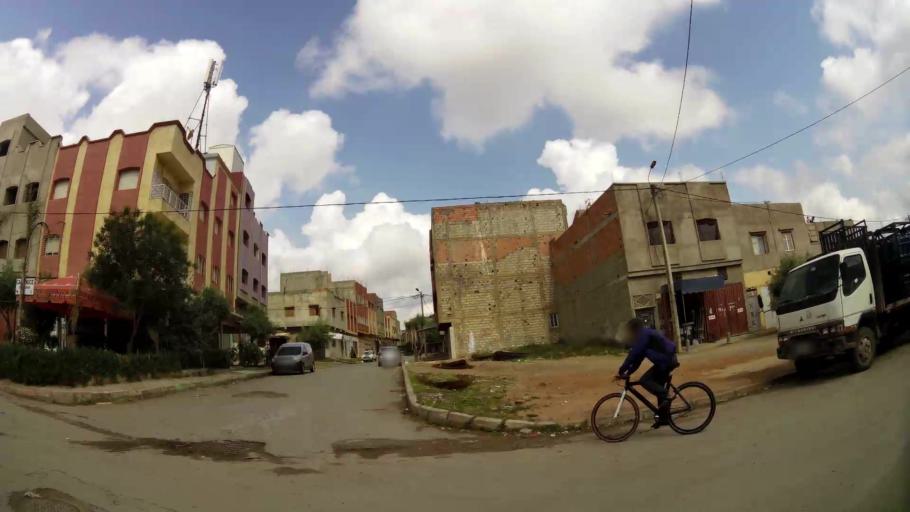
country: MA
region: Rabat-Sale-Zemmour-Zaer
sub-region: Khemisset
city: Tiflet
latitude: 33.8975
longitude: -6.3231
